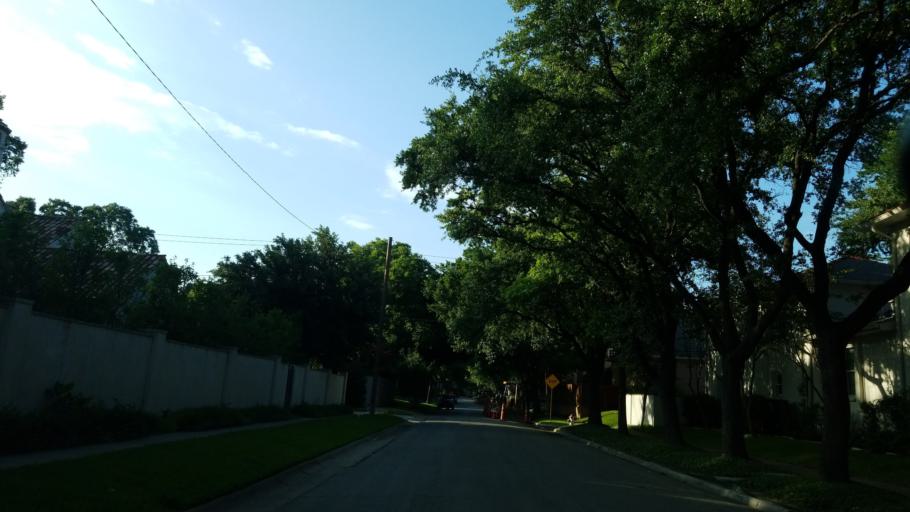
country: US
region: Texas
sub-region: Dallas County
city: University Park
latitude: 32.8453
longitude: -96.7928
